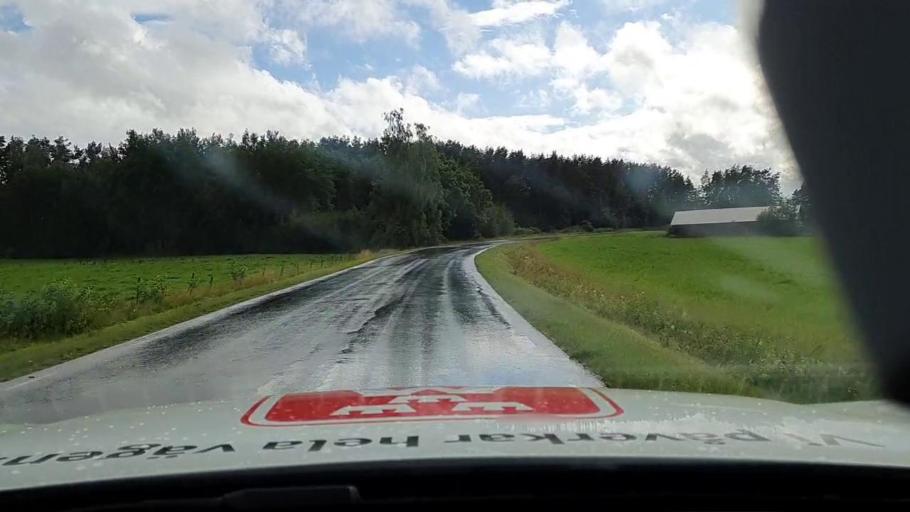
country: SE
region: Vaestra Goetaland
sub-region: Skovde Kommun
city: Stopen
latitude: 58.5297
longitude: 13.9435
